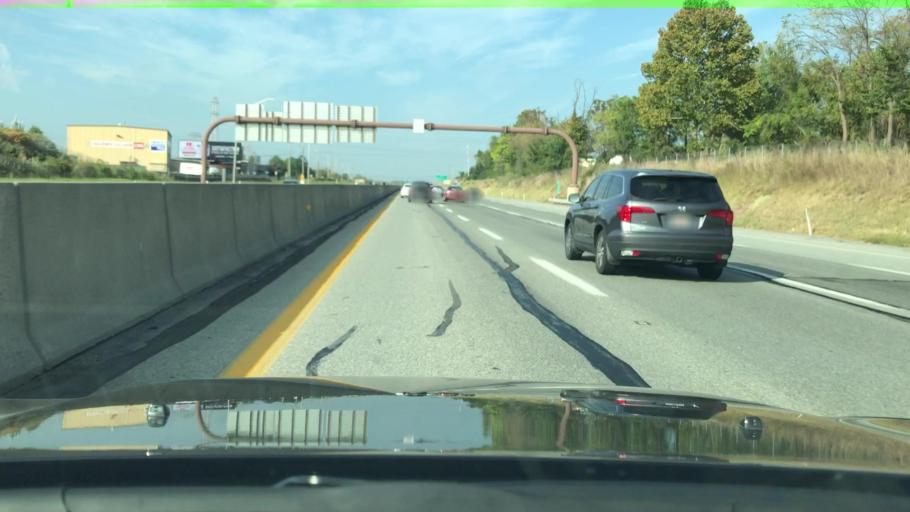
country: US
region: Pennsylvania
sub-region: Montgomery County
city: Plymouth Meeting
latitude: 40.1099
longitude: -75.2935
